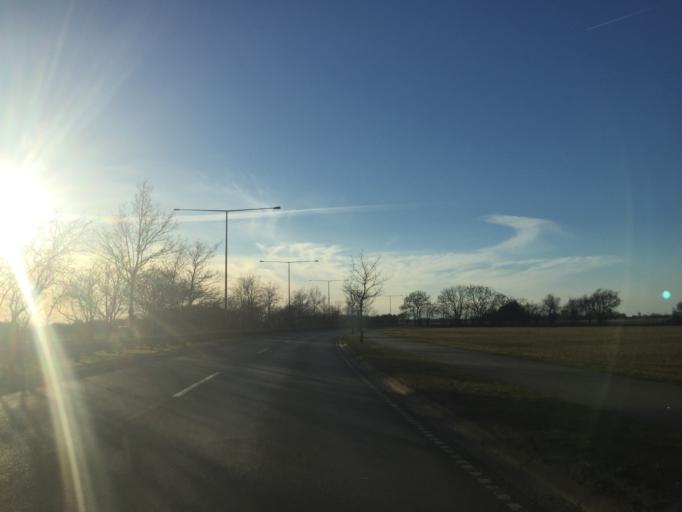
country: DK
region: Capital Region
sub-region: Dragor Kommune
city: Dragor
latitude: 55.5966
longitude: 12.6296
